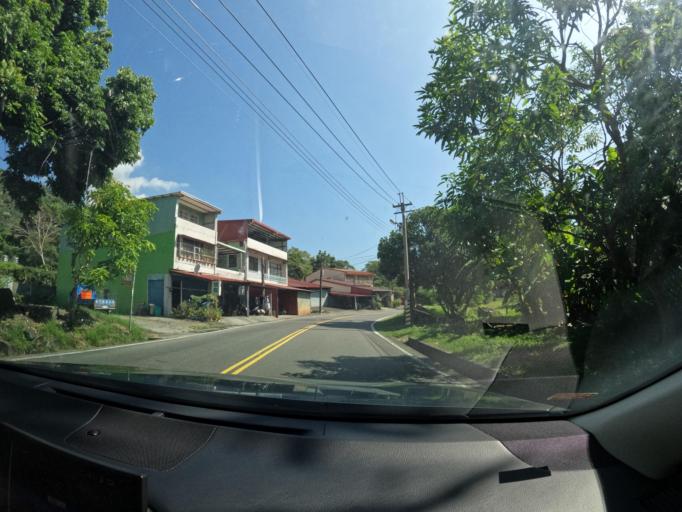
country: TW
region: Taiwan
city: Yujing
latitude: 23.1010
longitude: 120.6834
